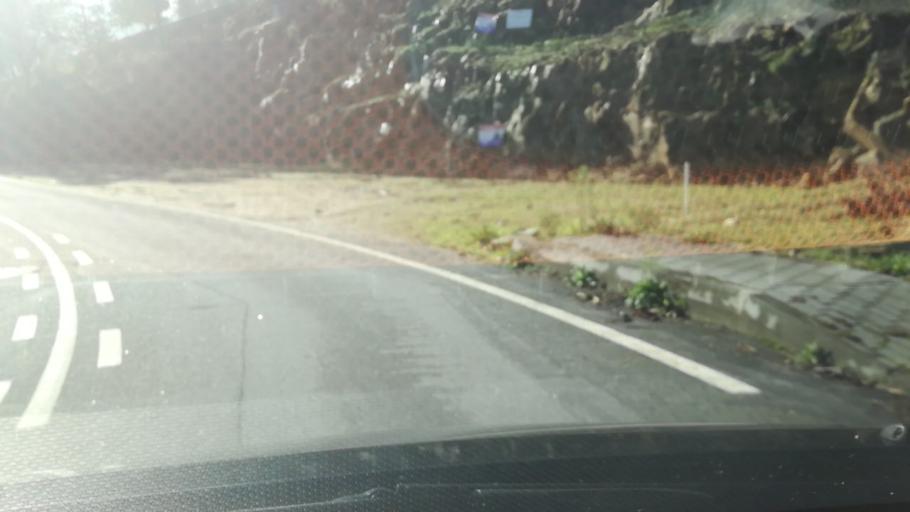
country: PT
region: Braga
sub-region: Guimaraes
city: Ponte
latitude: 41.5243
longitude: -8.3425
